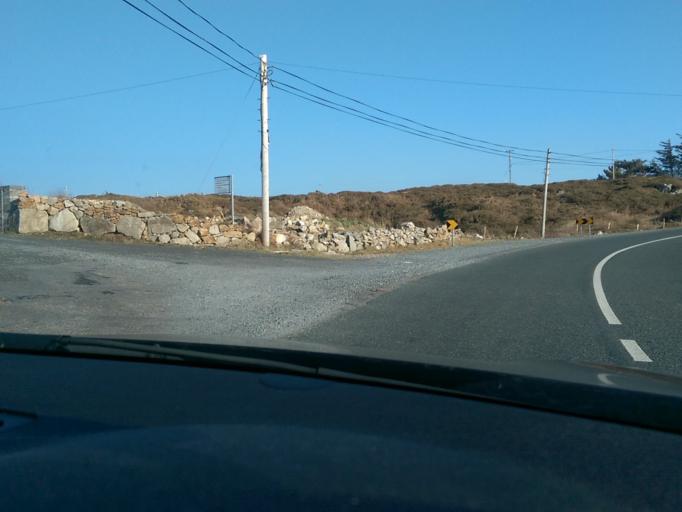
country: IE
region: Connaught
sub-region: County Galway
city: Clifden
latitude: 53.3176
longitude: -9.8052
